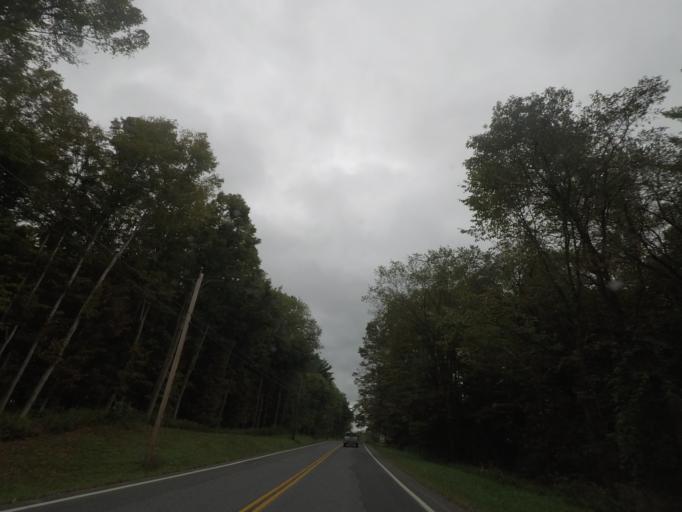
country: US
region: New York
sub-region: Washington County
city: Cambridge
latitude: 42.9535
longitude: -73.4301
